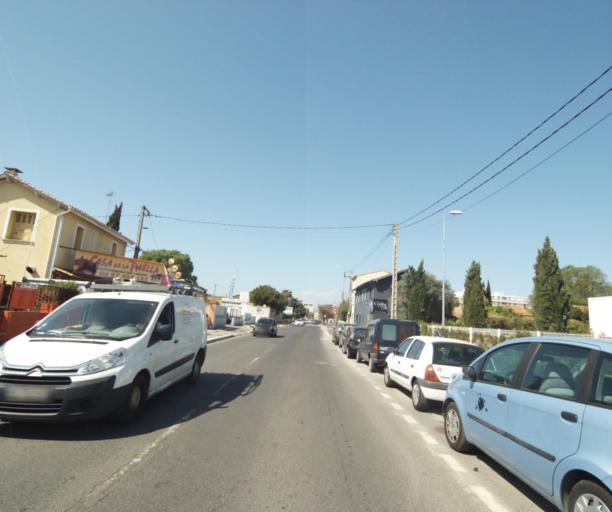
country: FR
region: Languedoc-Roussillon
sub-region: Departement de l'Herault
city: Montpellier
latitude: 43.6121
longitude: 3.8983
